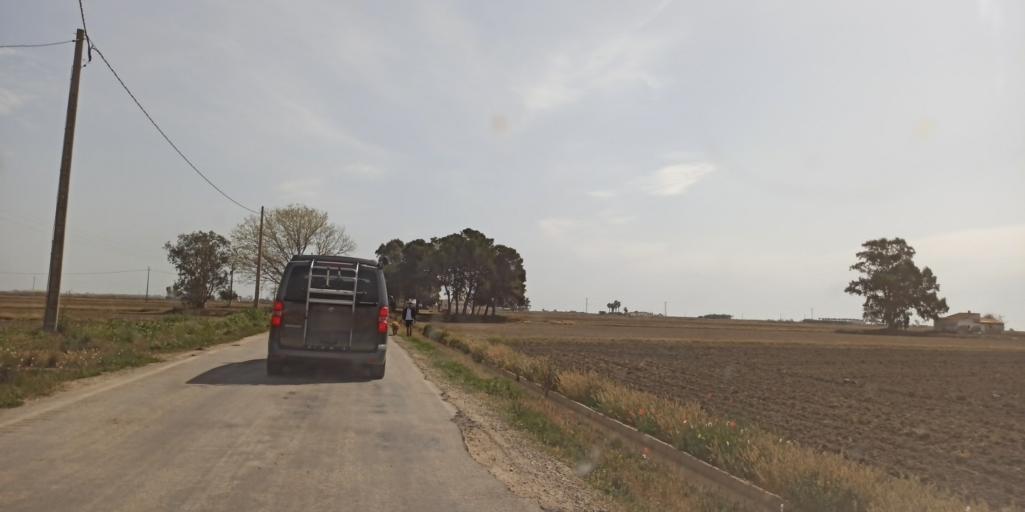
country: ES
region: Catalonia
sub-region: Provincia de Tarragona
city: Deltebre
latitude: 40.6465
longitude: 0.7109
